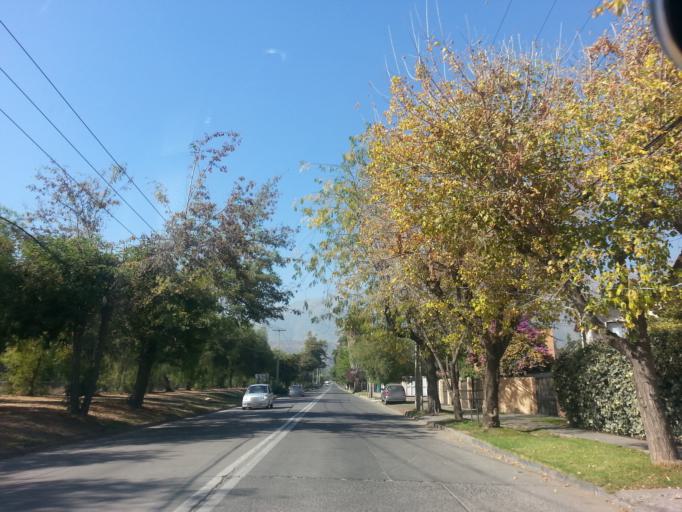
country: CL
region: Santiago Metropolitan
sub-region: Provincia de Santiago
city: Villa Presidente Frei, Nunoa, Santiago, Chile
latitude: -33.4348
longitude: -70.5493
